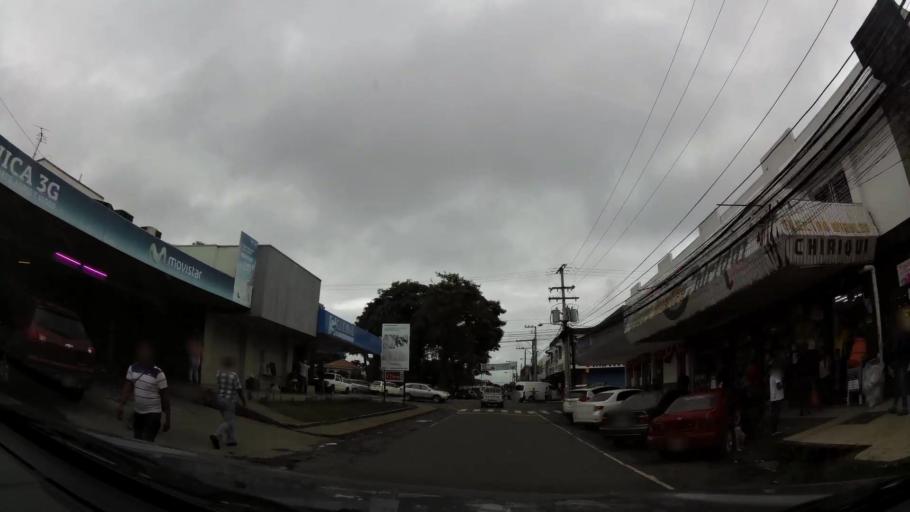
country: PA
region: Chiriqui
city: La Concepcion
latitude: 8.5172
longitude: -82.6207
